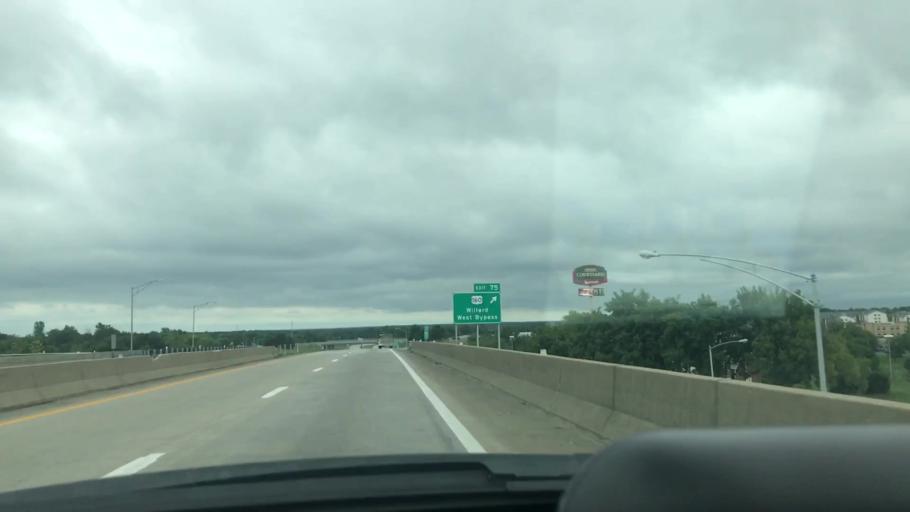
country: US
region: Missouri
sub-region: Greene County
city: Springfield
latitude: 37.2414
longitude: -93.3531
